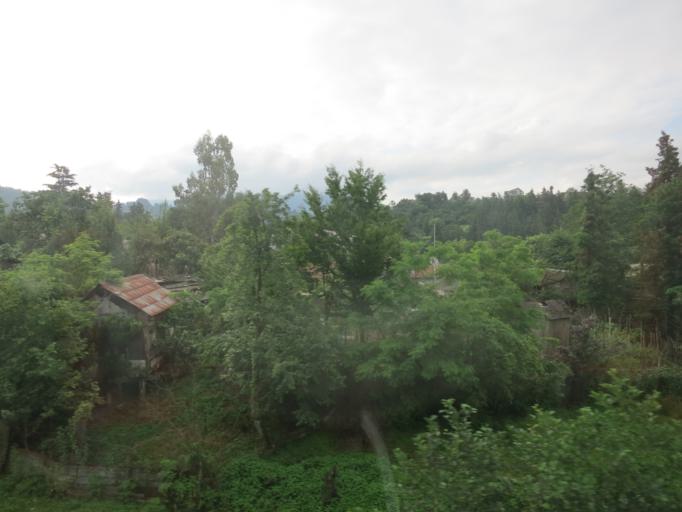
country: GE
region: Ajaria
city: Kobuleti
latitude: 41.7467
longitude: 41.7397
